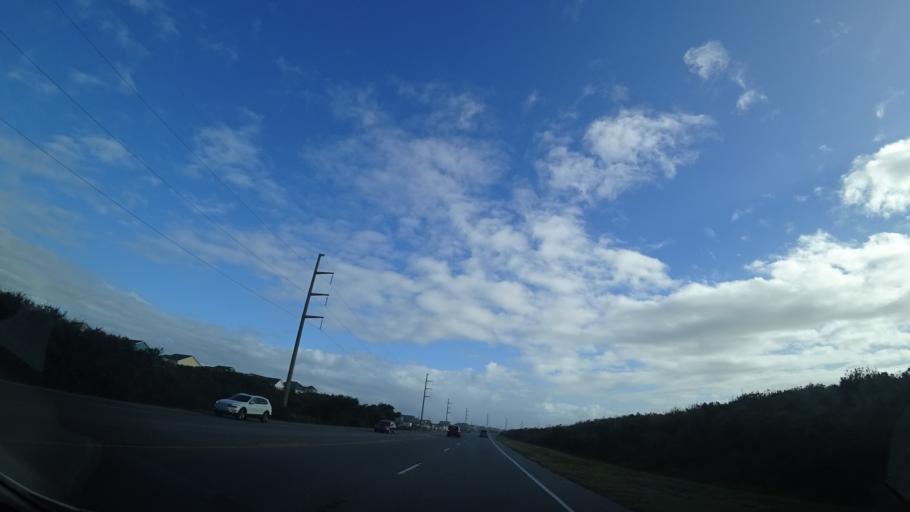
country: US
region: North Carolina
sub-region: Dare County
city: Nags Head
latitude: 35.9658
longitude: -75.6308
